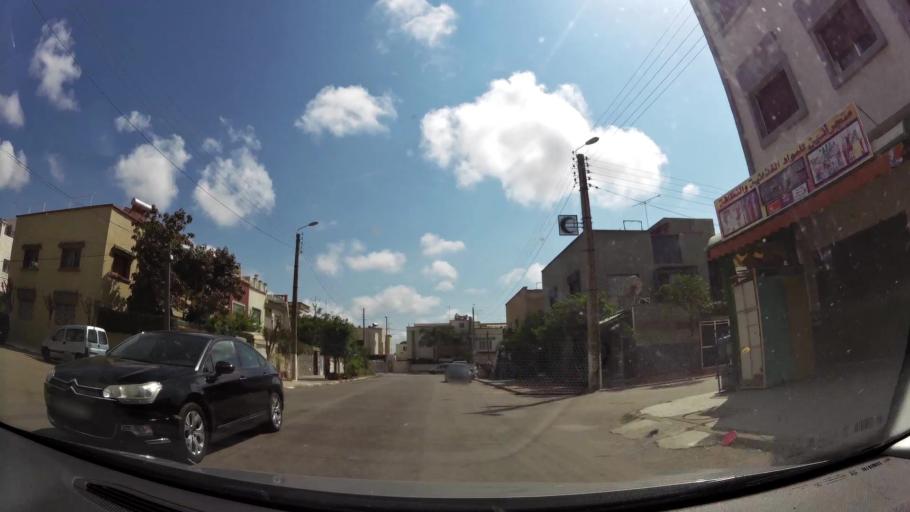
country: MA
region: Rabat-Sale-Zemmour-Zaer
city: Sale
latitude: 34.0403
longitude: -6.7913
